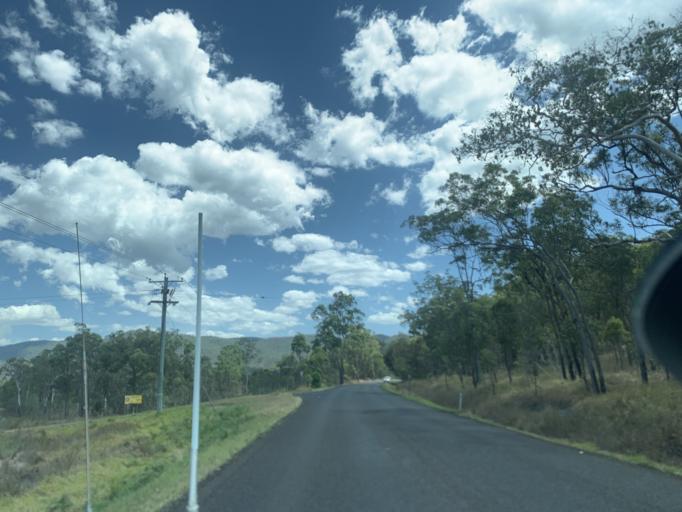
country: AU
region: Queensland
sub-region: Tablelands
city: Atherton
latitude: -17.3096
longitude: 145.4565
